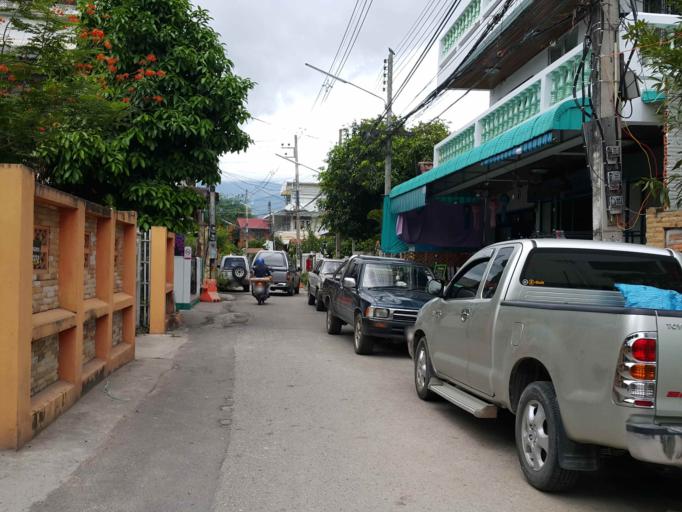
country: TH
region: Chiang Mai
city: Chiang Mai
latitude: 18.7941
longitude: 98.9912
